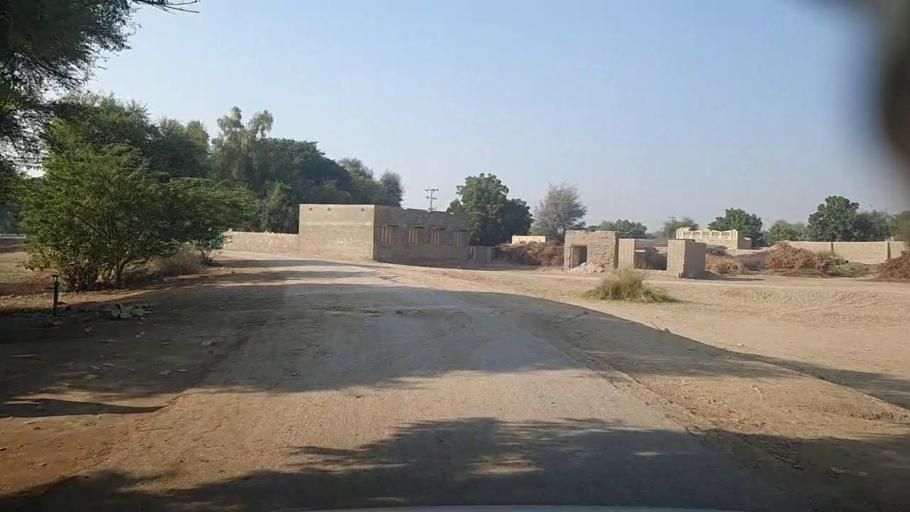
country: PK
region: Sindh
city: Karaundi
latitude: 26.7886
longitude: 68.4668
